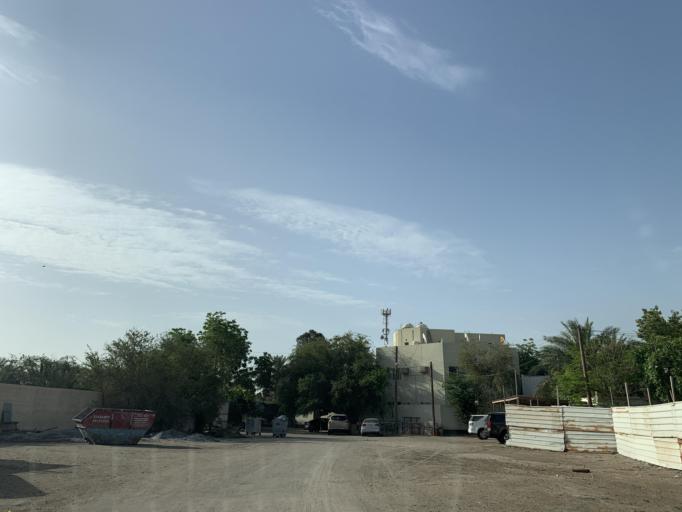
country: BH
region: Manama
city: Manama
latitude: 26.1822
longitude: 50.5853
